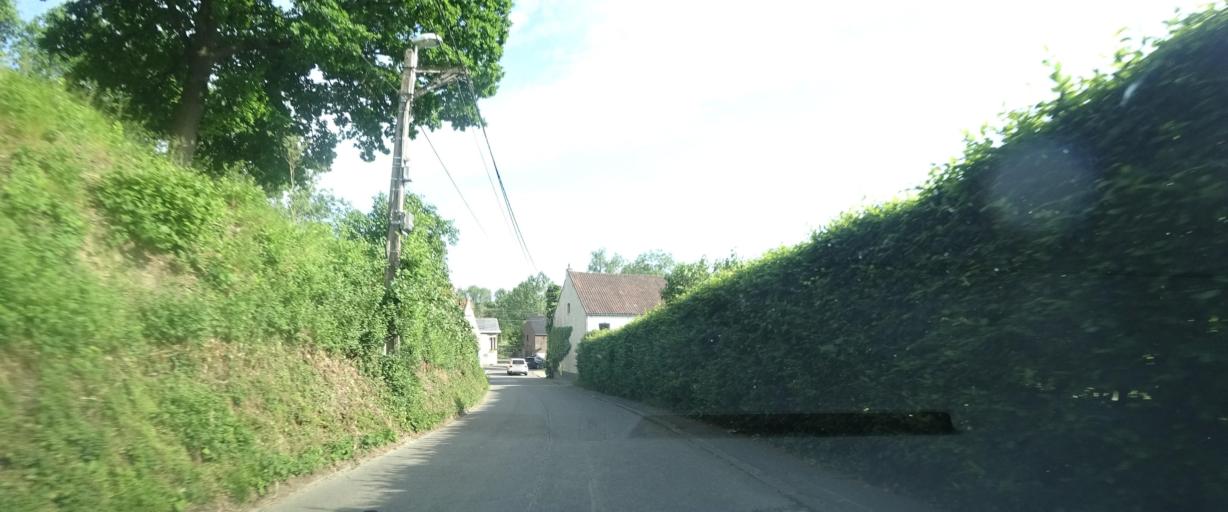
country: BE
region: Wallonia
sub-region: Province du Brabant Wallon
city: Grez-Doiceau
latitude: 50.7003
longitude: 4.6619
